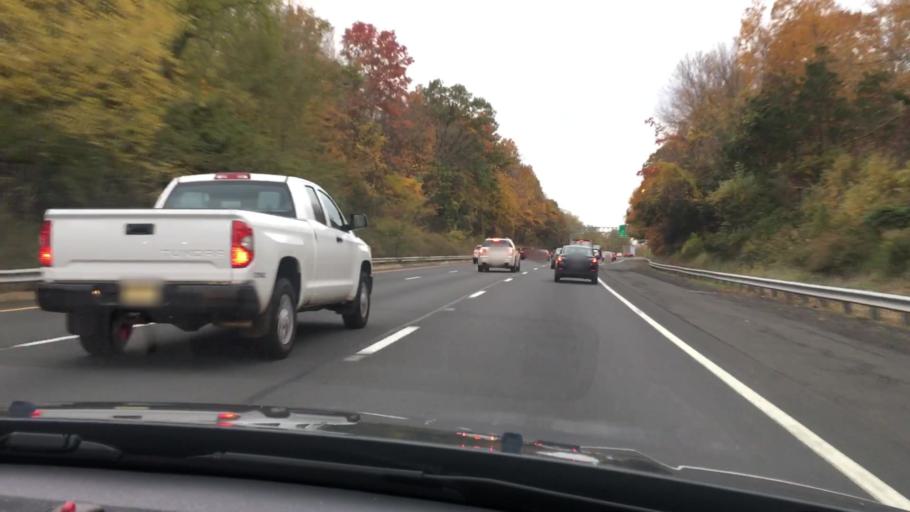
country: US
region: New Jersey
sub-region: Somerset County
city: Bernardsville
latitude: 40.6931
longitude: -74.5712
